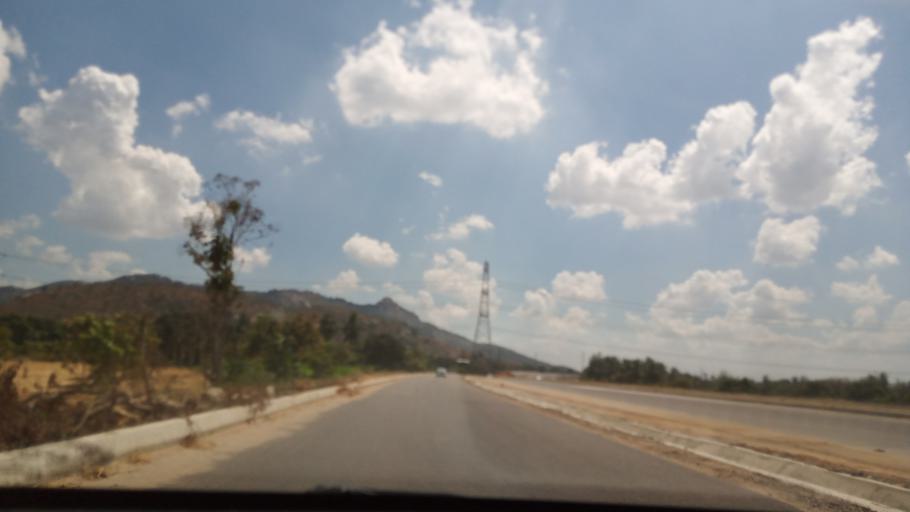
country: IN
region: Andhra Pradesh
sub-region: Chittoor
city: Pakala
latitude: 13.3425
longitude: 79.0818
